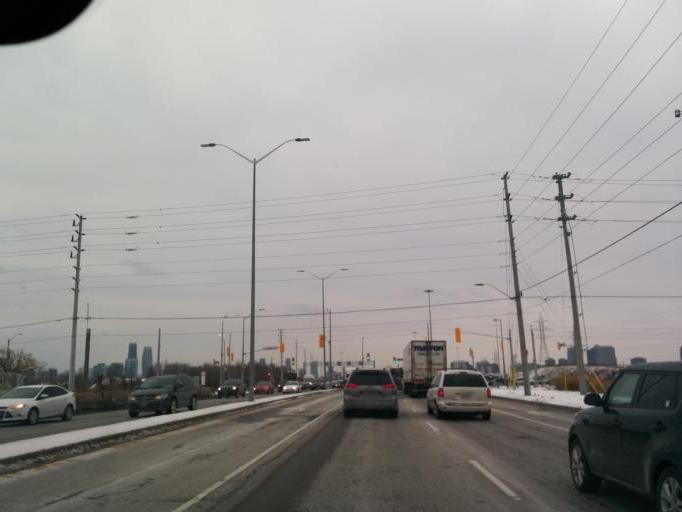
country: CA
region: Ontario
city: Mississauga
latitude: 43.6166
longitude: -79.6278
